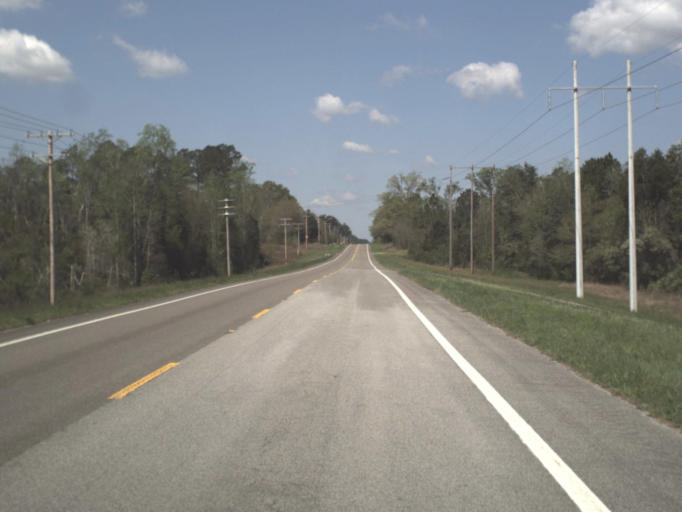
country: US
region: Florida
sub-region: Santa Rosa County
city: Point Baker
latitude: 30.8634
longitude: -86.9052
